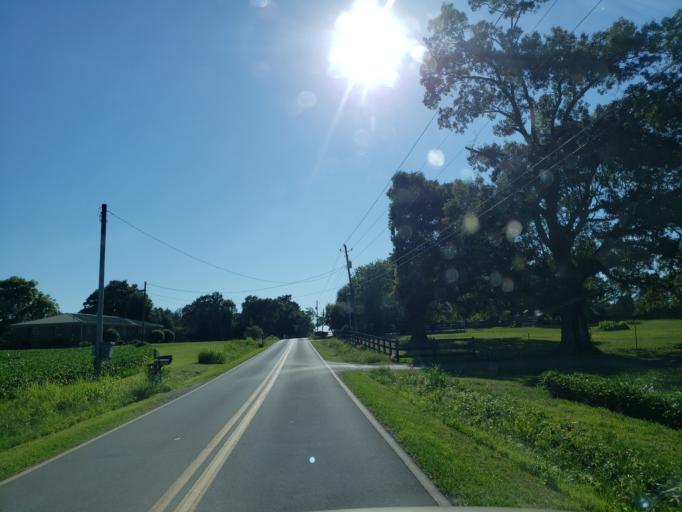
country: US
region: Georgia
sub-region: Bartow County
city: Euharlee
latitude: 34.1085
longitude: -84.9251
